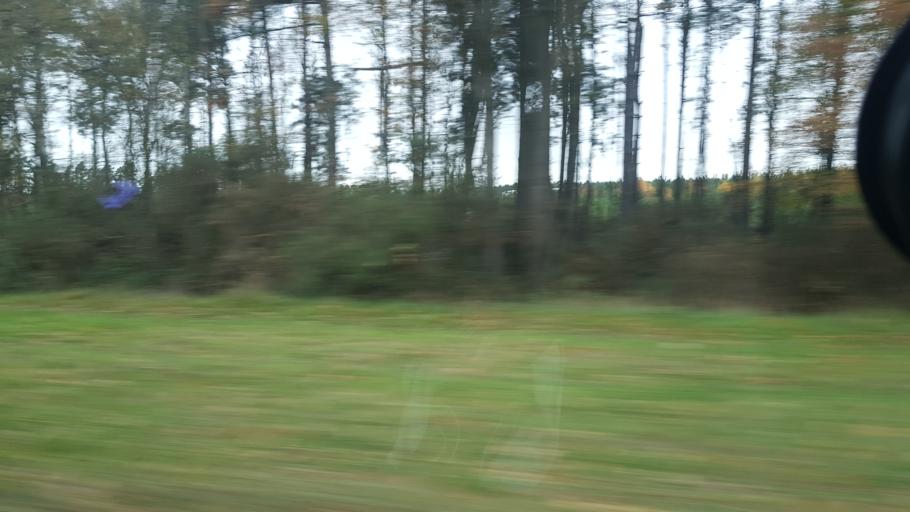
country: GB
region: England
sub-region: Hampshire
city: Eversley
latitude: 51.3202
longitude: -0.8654
